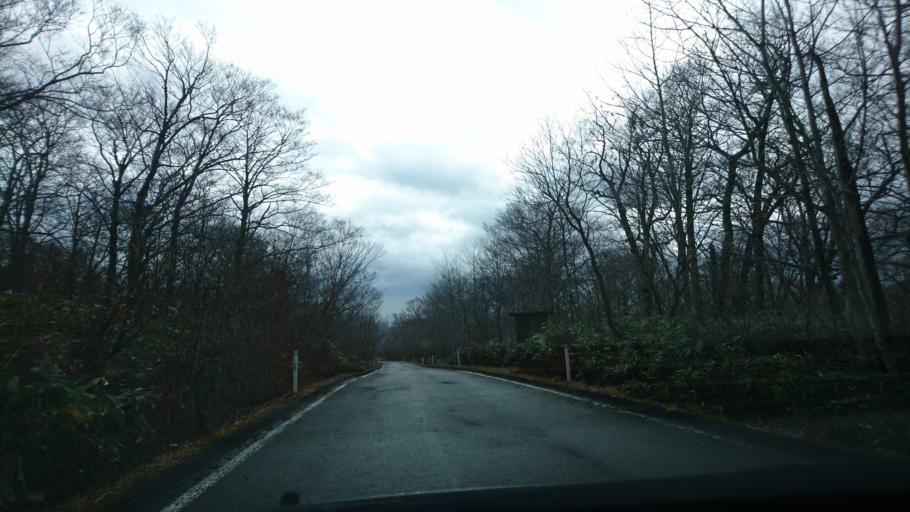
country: JP
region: Iwate
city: Ichinoseki
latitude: 38.9427
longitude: 140.8166
